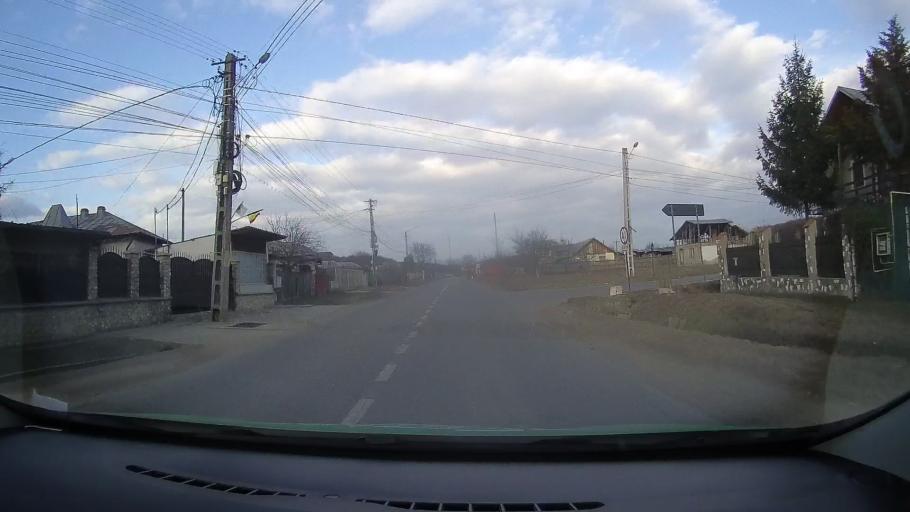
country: RO
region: Dambovita
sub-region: Comuna Gura Ocnitei
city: Gura Ocnitei
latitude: 44.9391
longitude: 25.5791
